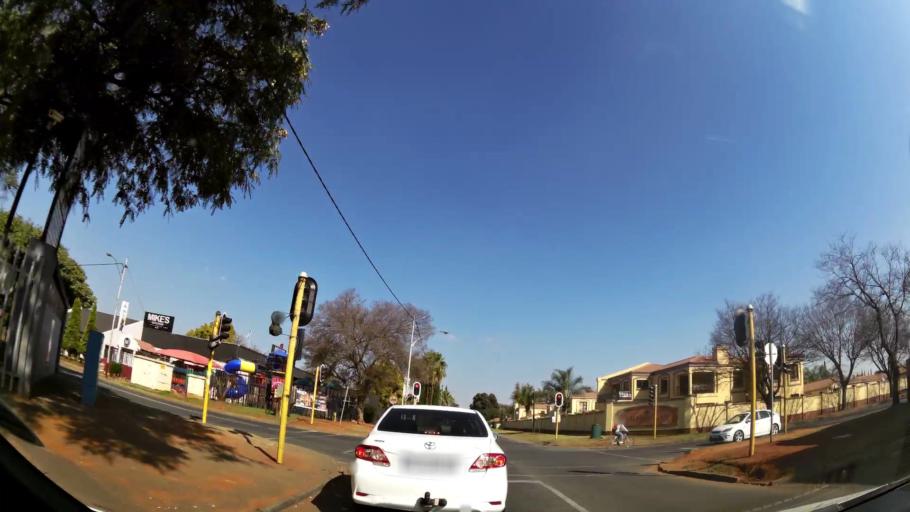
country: ZA
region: Gauteng
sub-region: Ekurhuleni Metropolitan Municipality
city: Boksburg
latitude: -26.1844
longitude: 28.2761
